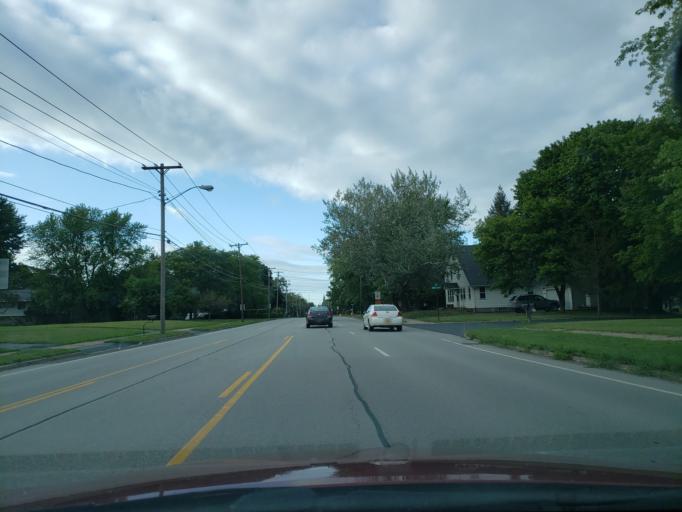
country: US
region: New York
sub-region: Monroe County
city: Greece
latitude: 43.2420
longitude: -77.6591
